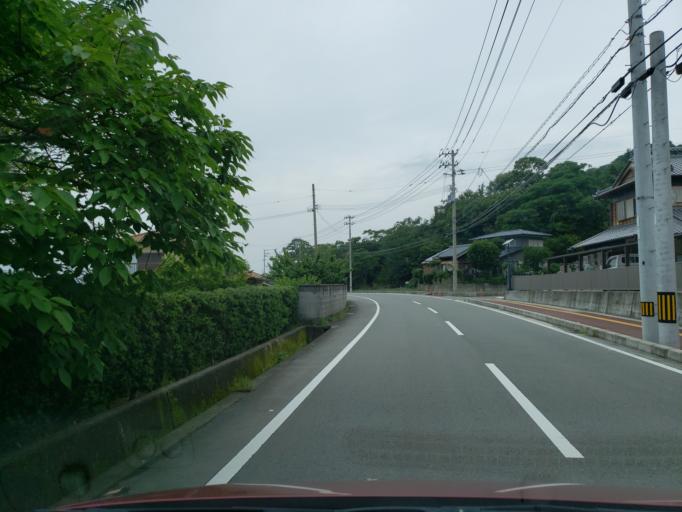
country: JP
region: Tokushima
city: Kamojimacho-jogejima
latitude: 34.1017
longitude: 134.2947
